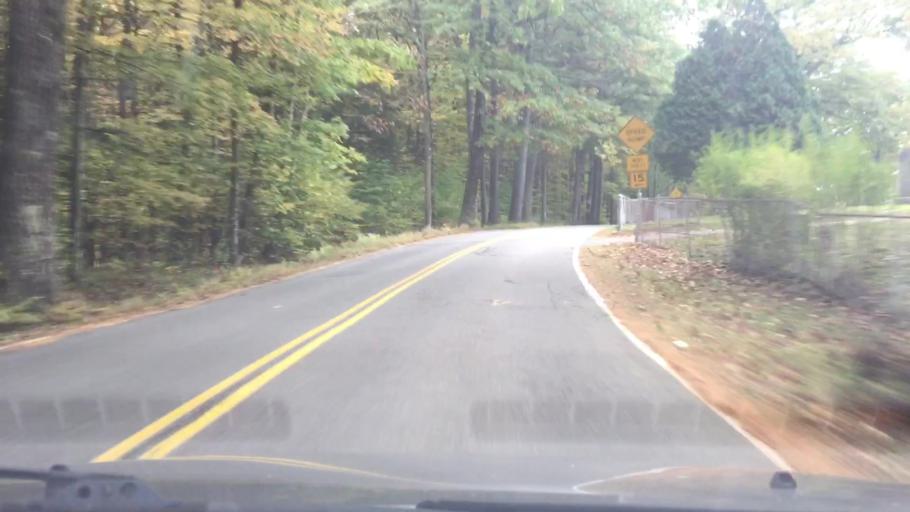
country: US
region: New Hampshire
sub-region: Cheshire County
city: Keene
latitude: 42.9437
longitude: -72.2661
